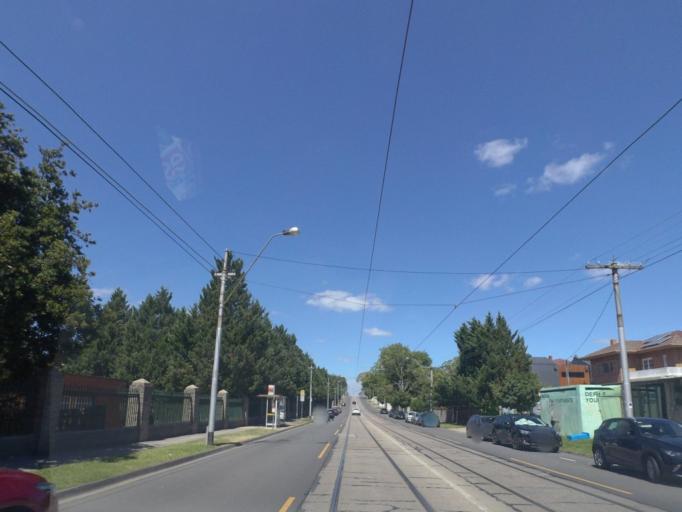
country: AU
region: Victoria
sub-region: Boroondara
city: Kew East
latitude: -37.8095
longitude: 145.0538
